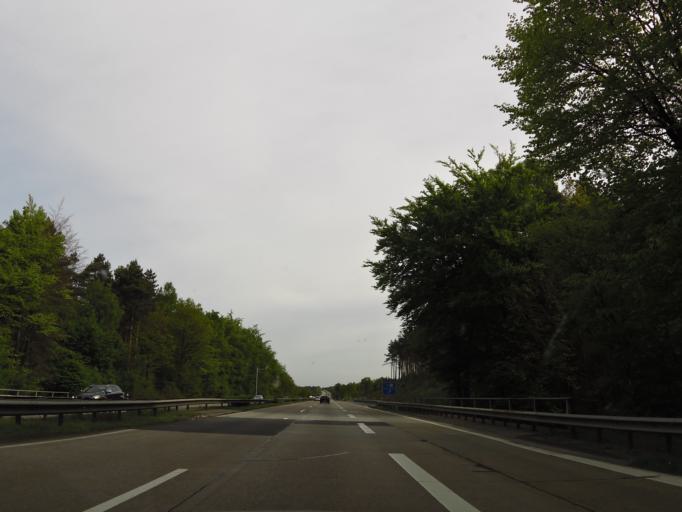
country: DE
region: Lower Saxony
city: Bad Fallingbostel
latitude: 52.8053
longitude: 9.6783
